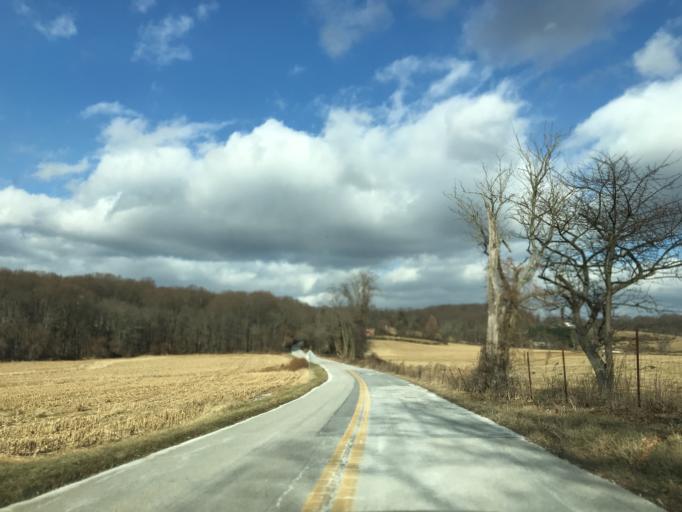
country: US
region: Maryland
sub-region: Baltimore County
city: Hunt Valley
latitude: 39.5754
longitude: -76.6565
